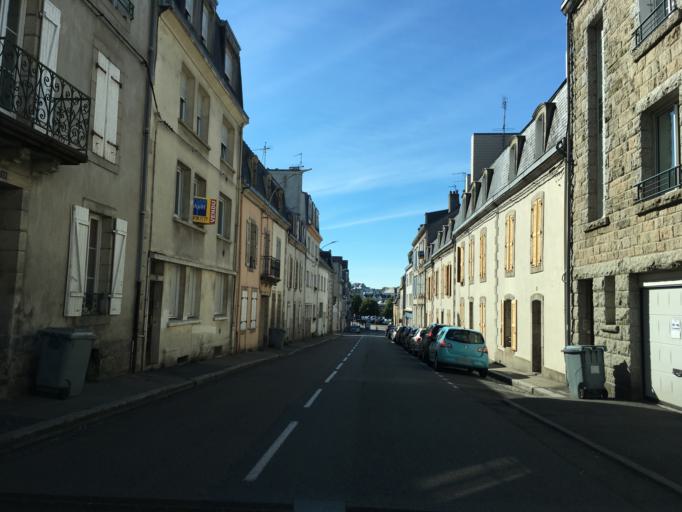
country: FR
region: Brittany
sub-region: Departement du Finistere
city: Quimper
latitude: 47.9931
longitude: -4.0902
